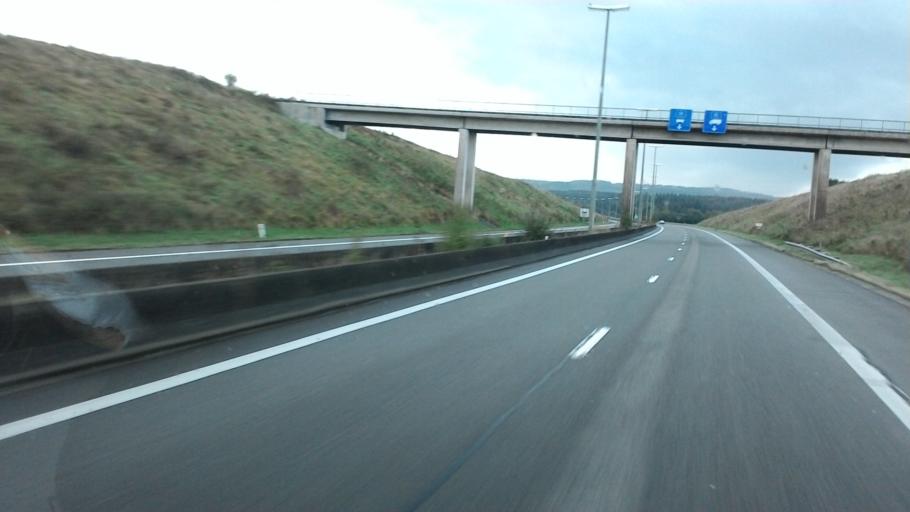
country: BE
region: Wallonia
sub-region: Province du Luxembourg
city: Houffalize
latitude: 50.1581
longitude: 5.7945
